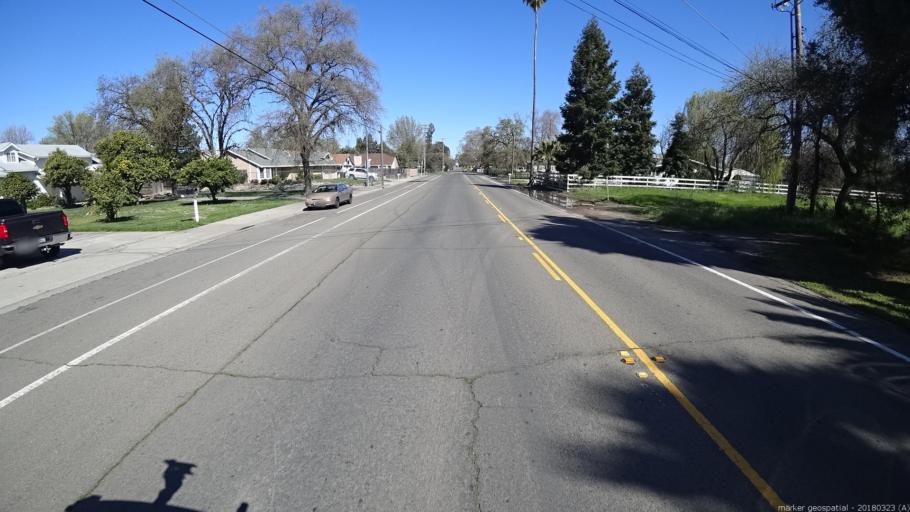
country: US
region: California
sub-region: Sacramento County
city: Rio Linda
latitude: 38.6936
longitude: -121.4384
